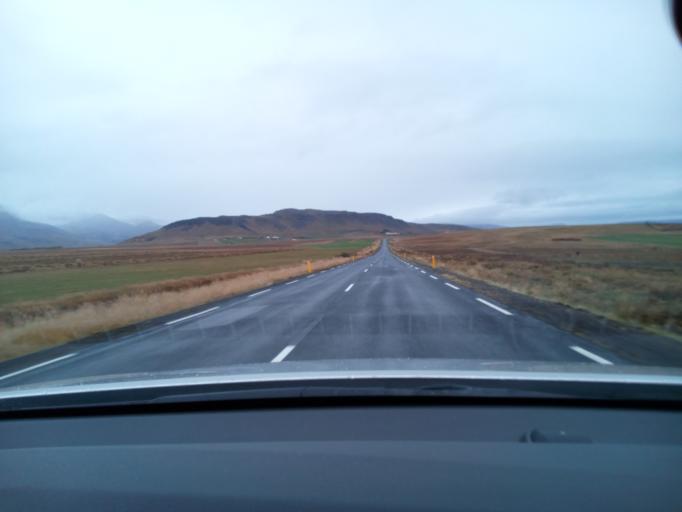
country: IS
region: West
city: Borgarnes
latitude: 64.3913
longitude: -21.8088
